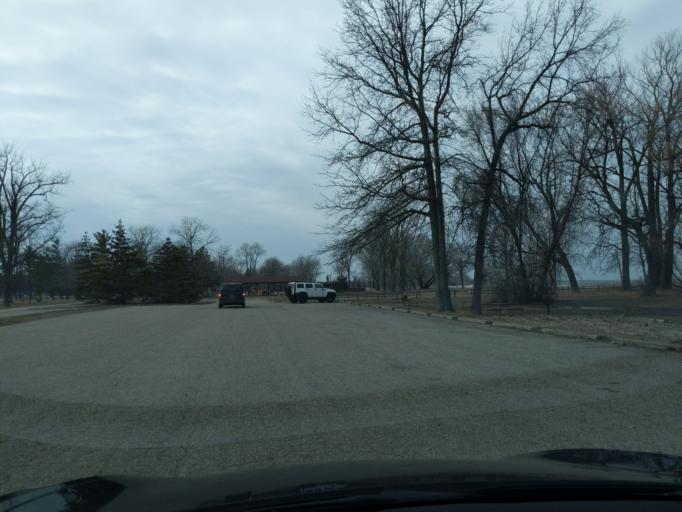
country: US
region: Michigan
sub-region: Bay County
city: Bay City
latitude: 43.6668
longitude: -83.9018
